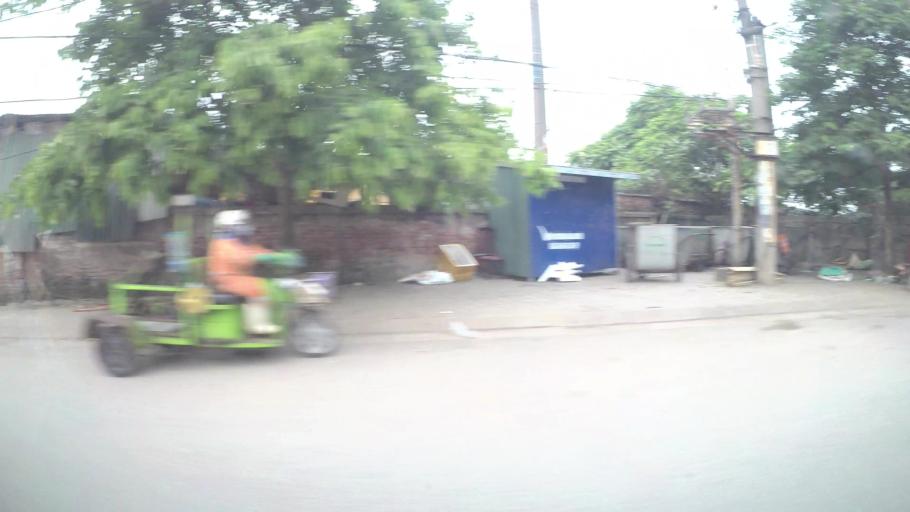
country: VN
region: Ha Noi
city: Hoan Kiem
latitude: 21.0655
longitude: 105.8857
